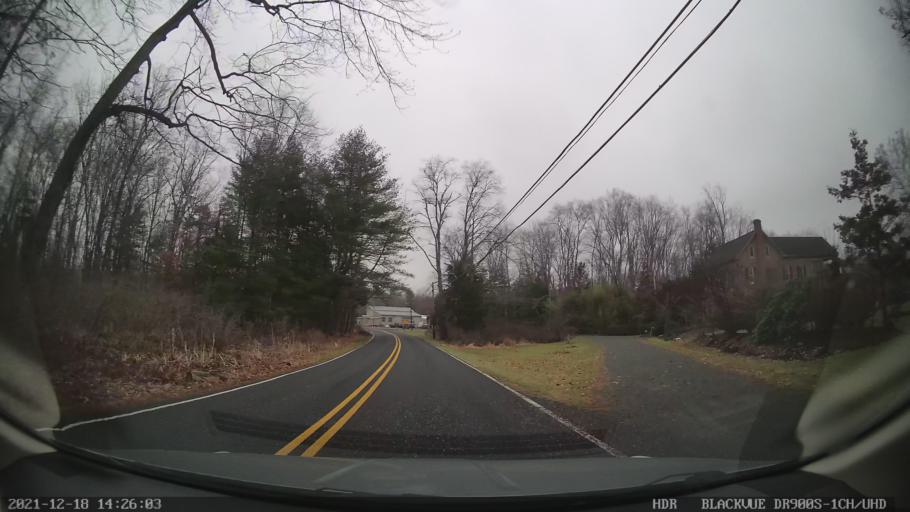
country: US
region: Pennsylvania
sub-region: Berks County
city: Oley
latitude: 40.4106
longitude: -75.7380
